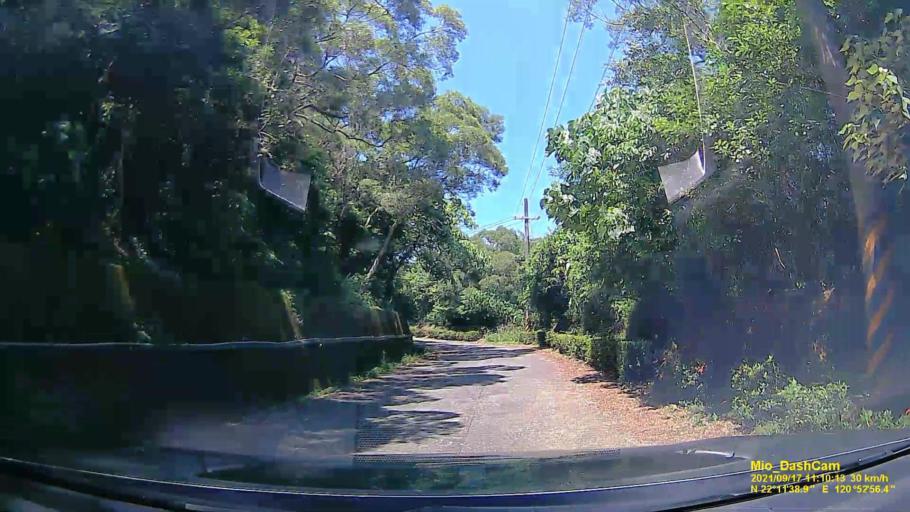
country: TW
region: Taiwan
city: Hengchun
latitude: 22.1942
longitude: 120.8823
